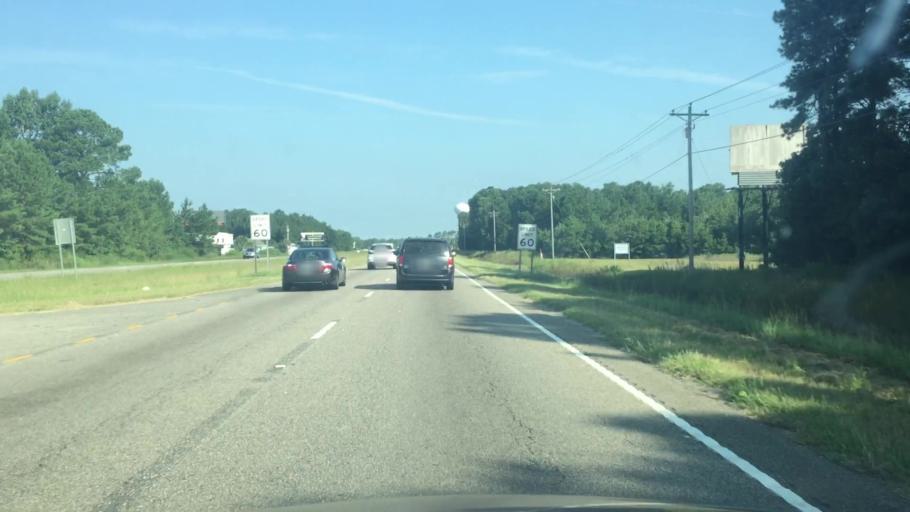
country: US
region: South Carolina
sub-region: Horry County
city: North Myrtle Beach
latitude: 33.8950
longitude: -78.6944
